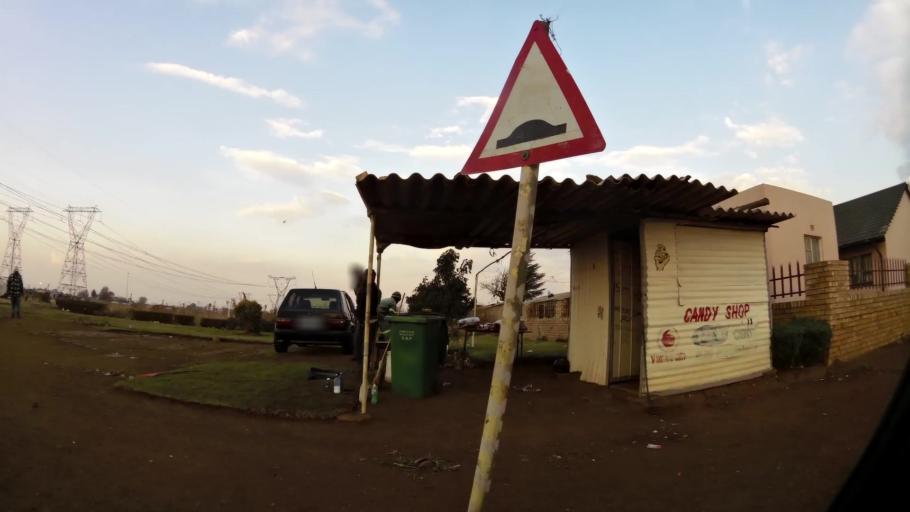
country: ZA
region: Gauteng
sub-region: City of Johannesburg Metropolitan Municipality
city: Orange Farm
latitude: -26.5571
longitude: 27.8390
